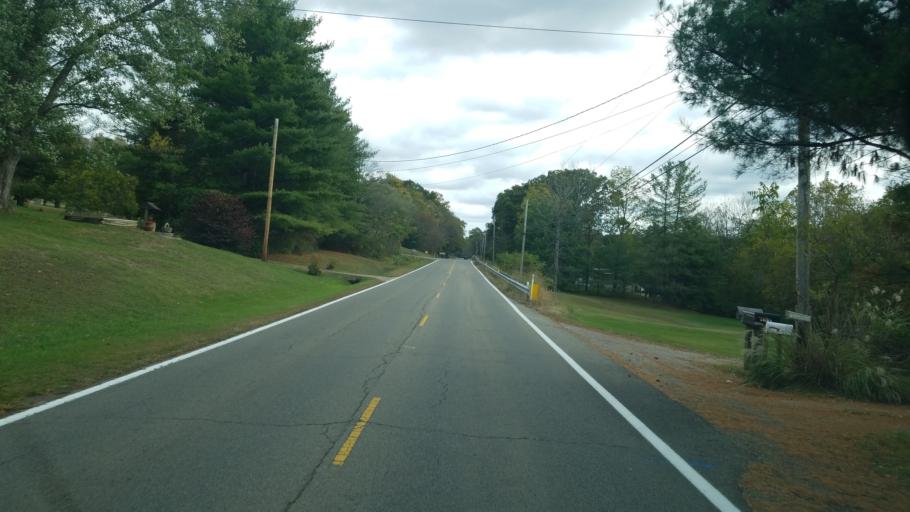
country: US
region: Ohio
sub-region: Jackson County
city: Wellston
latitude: 39.1169
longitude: -82.5645
